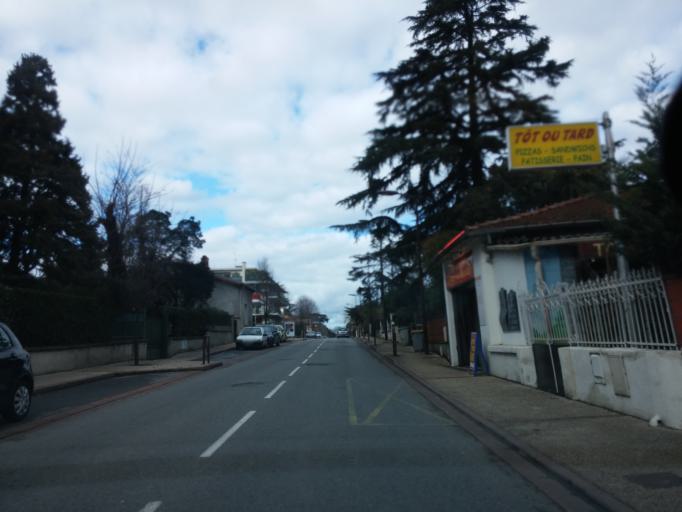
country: FR
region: Midi-Pyrenees
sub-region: Departement de la Haute-Garonne
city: Blagnac
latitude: 43.6255
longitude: 1.3988
